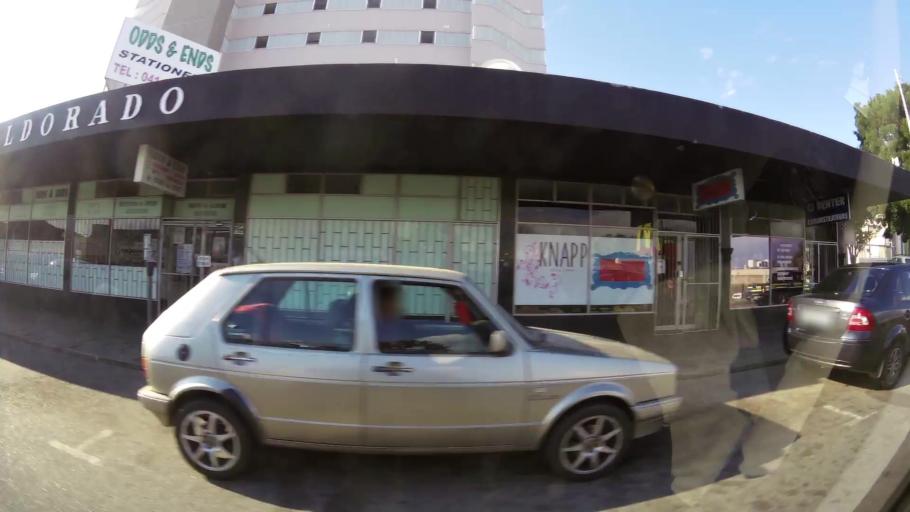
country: ZA
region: Eastern Cape
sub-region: Nelson Mandela Bay Metropolitan Municipality
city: Uitenhage
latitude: -33.7658
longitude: 25.3985
